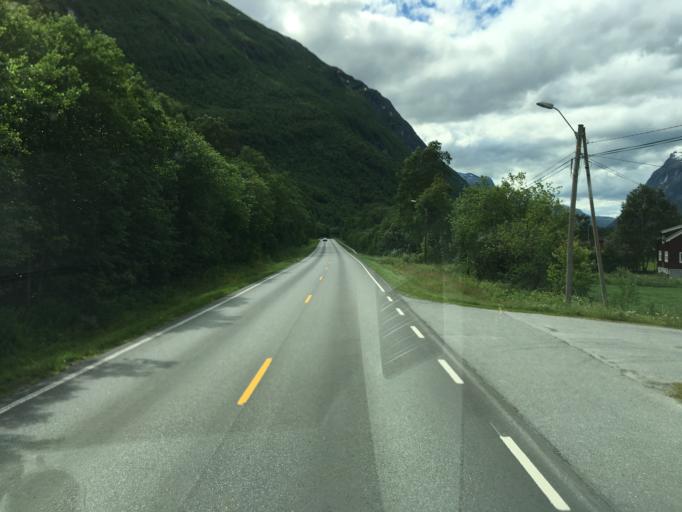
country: NO
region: More og Romsdal
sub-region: Sunndal
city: Sunndalsora
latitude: 62.6338
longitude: 8.8260
